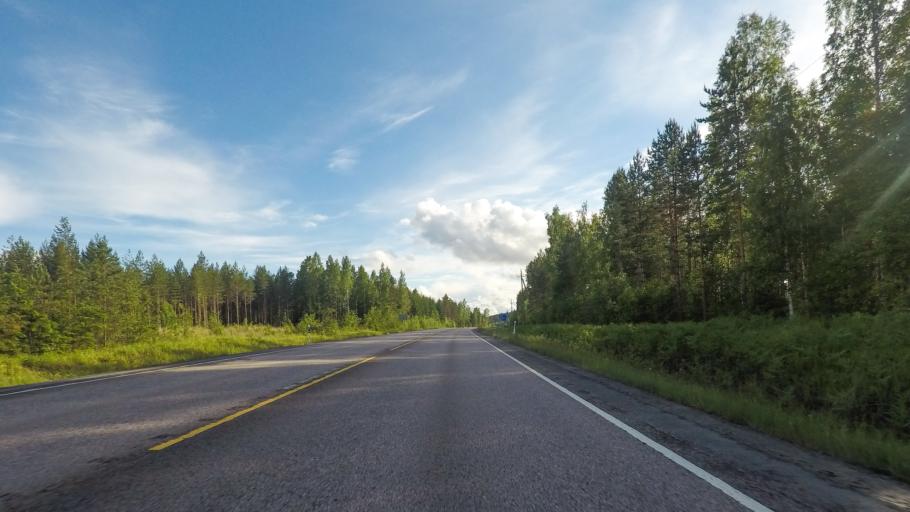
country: FI
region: Central Finland
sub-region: Joutsa
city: Joutsa
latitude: 61.7184
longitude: 26.0780
